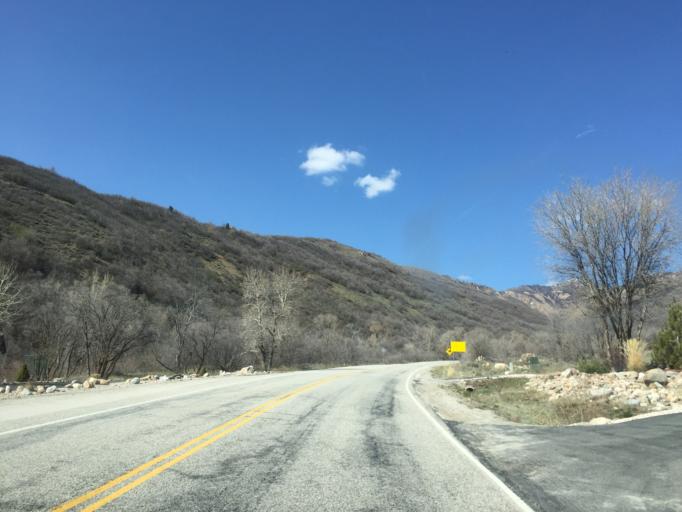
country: US
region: Utah
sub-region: Weber County
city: Wolf Creek
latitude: 41.3402
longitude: -111.8255
